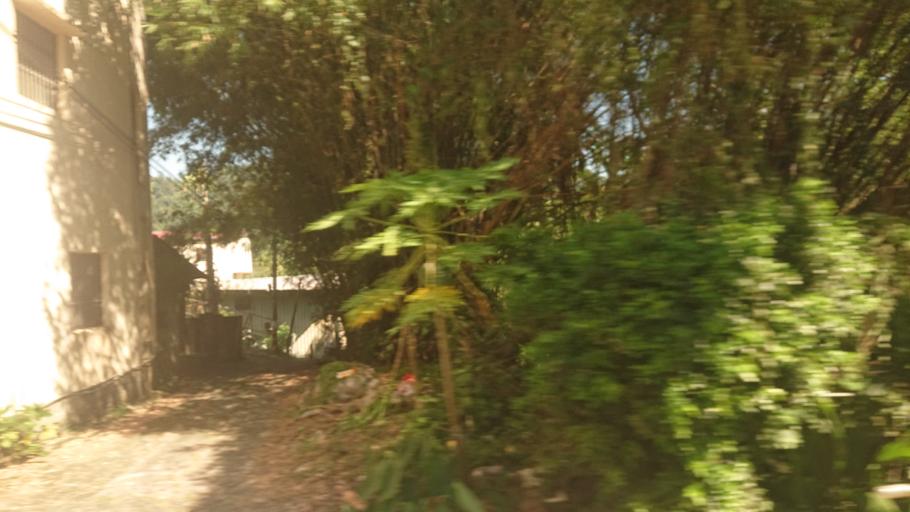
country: TW
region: Taiwan
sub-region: Nantou
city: Puli
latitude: 24.0615
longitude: 120.9428
